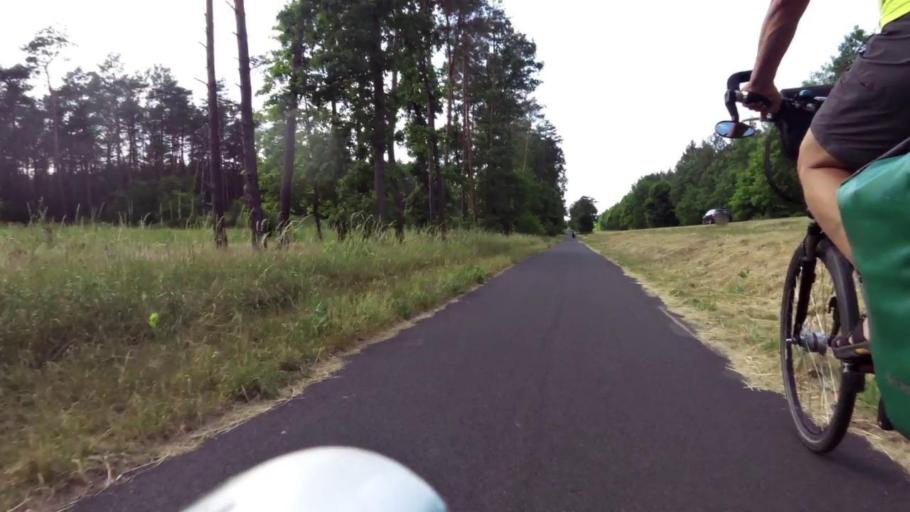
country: PL
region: Kujawsko-Pomorskie
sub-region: Powiat torunski
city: Lysomice
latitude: 53.0728
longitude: 18.5447
